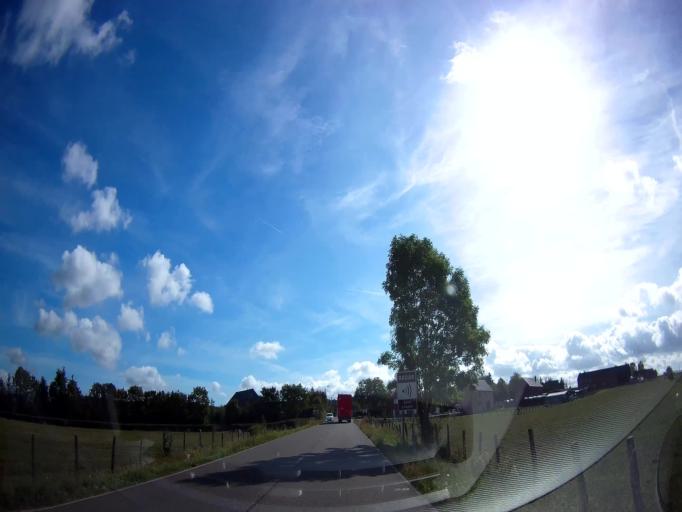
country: BE
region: Wallonia
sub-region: Province de Namur
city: Rochefort
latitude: 50.1672
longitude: 5.2028
